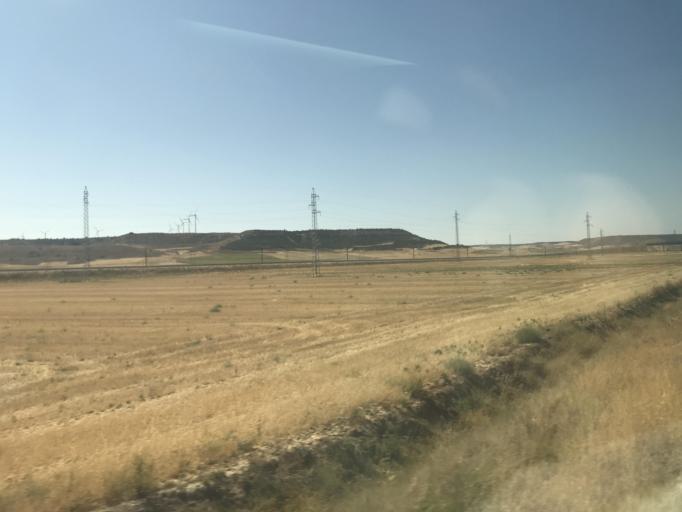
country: ES
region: Castille and Leon
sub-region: Provincia de Palencia
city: Torquemada
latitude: 42.0100
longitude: -4.3109
